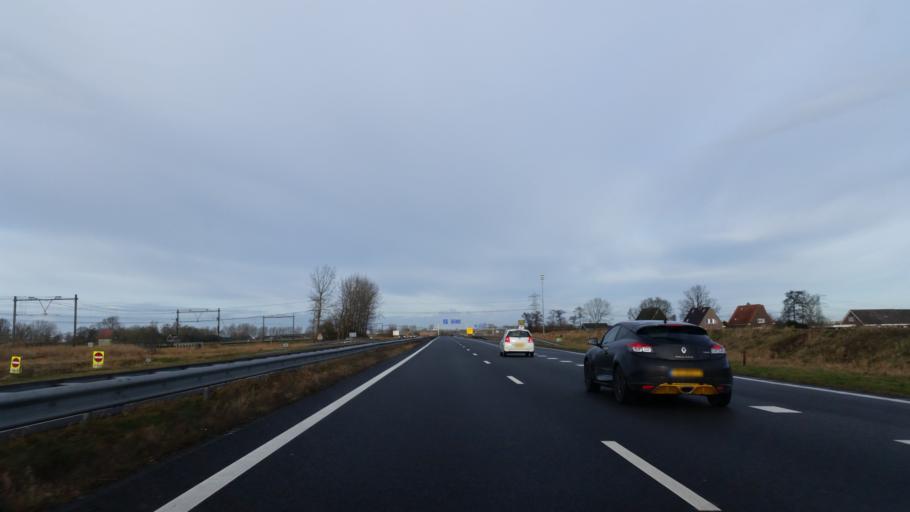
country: NL
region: Friesland
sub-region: Gemeente Leeuwarden
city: Wirdum
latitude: 53.1454
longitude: 5.7960
